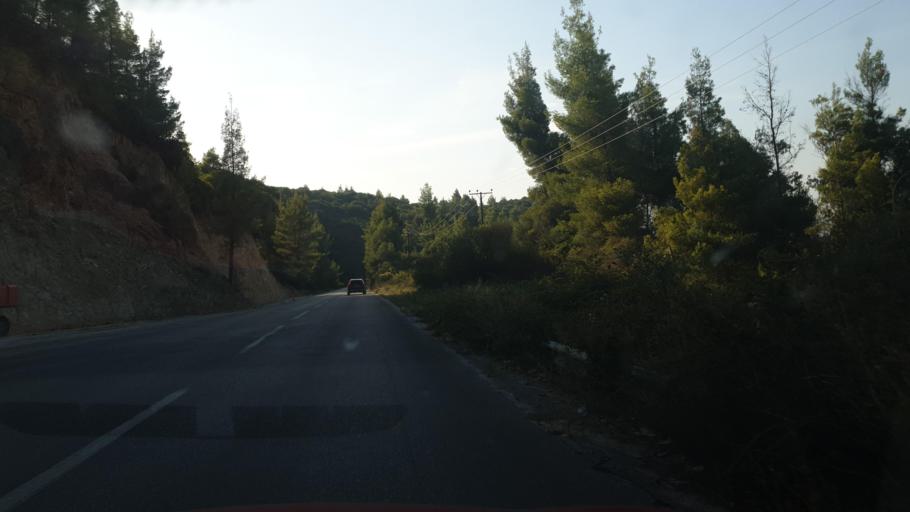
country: GR
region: Central Macedonia
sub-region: Nomos Chalkidikis
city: Neos Marmaras
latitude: 40.1625
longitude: 23.8691
